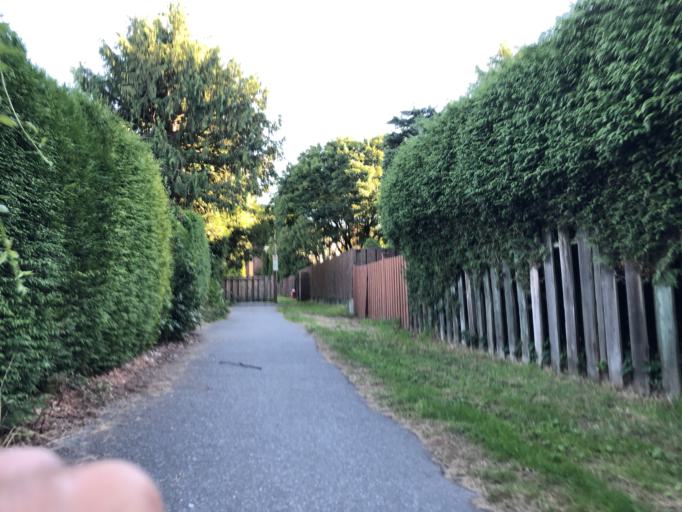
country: CA
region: British Columbia
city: Richmond
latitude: 49.1373
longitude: -123.1225
